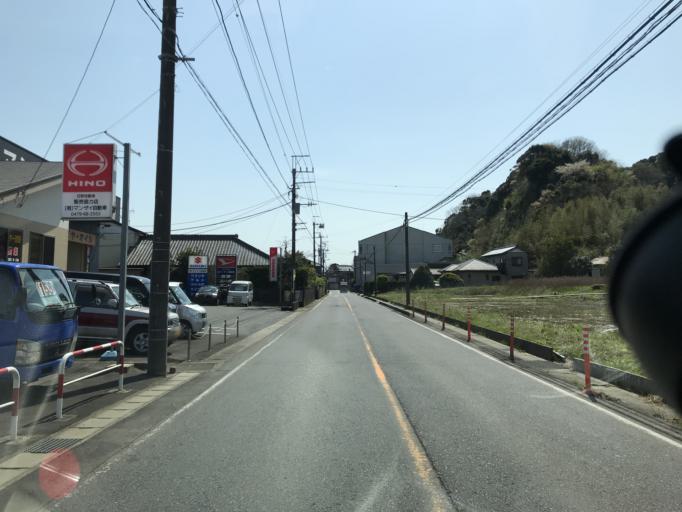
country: JP
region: Chiba
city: Asahi
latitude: 35.7798
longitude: 140.6491
